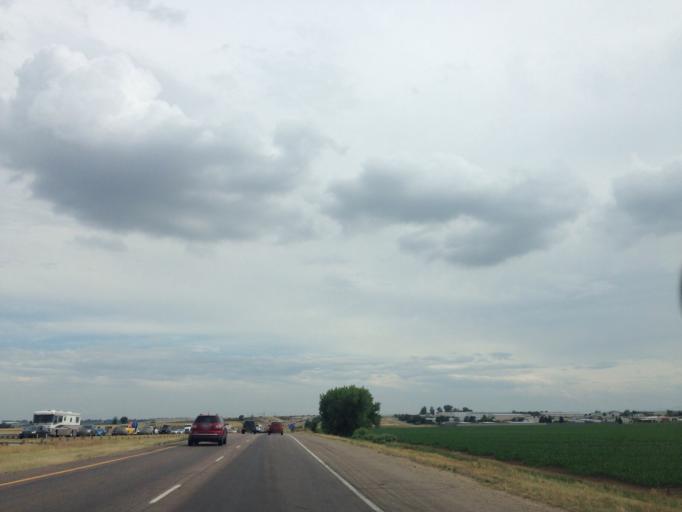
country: US
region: Colorado
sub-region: Weld County
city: Johnstown
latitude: 40.3487
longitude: -104.9812
